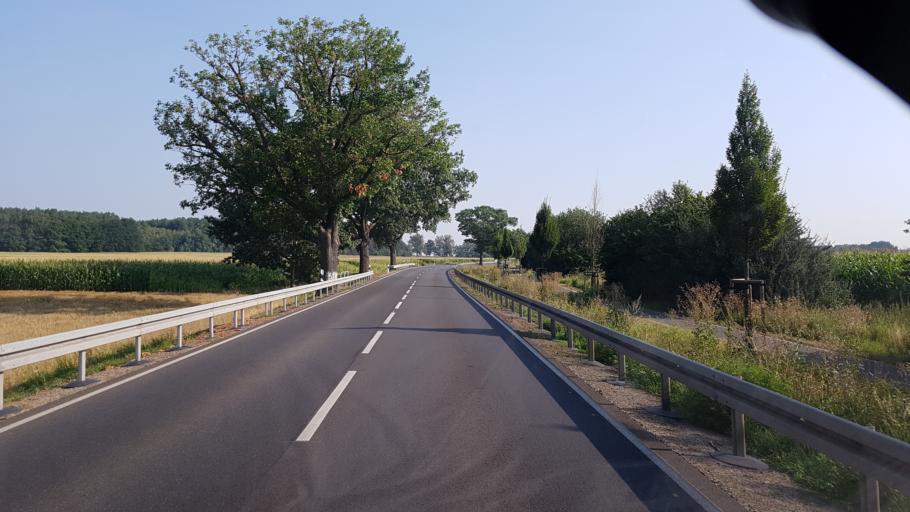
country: DE
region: Brandenburg
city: Kolkwitz
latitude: 51.7033
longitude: 14.2797
